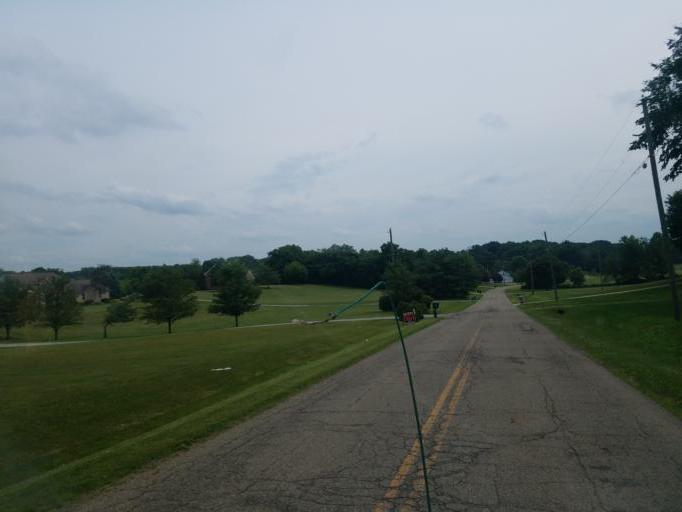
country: US
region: Ohio
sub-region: Knox County
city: Fredericktown
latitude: 40.4830
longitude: -82.5281
